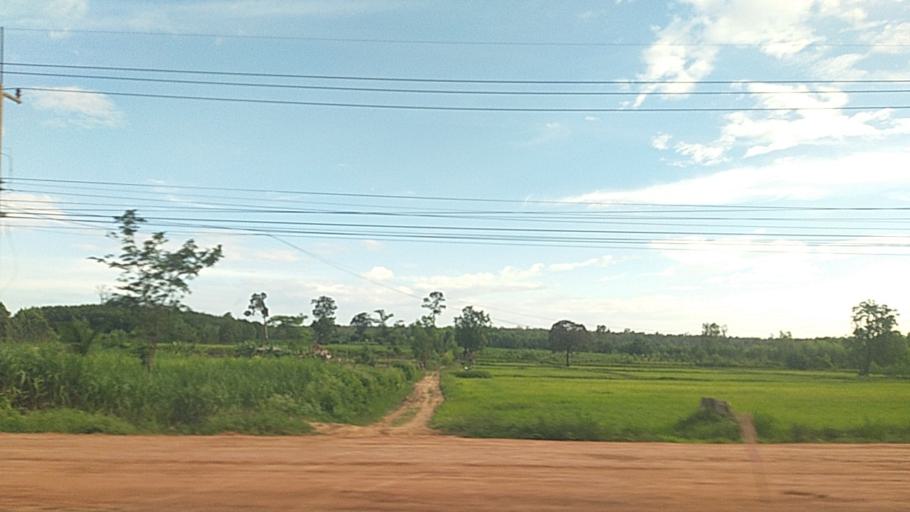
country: TH
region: Surin
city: Kap Choeng
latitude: 14.4616
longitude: 103.6551
